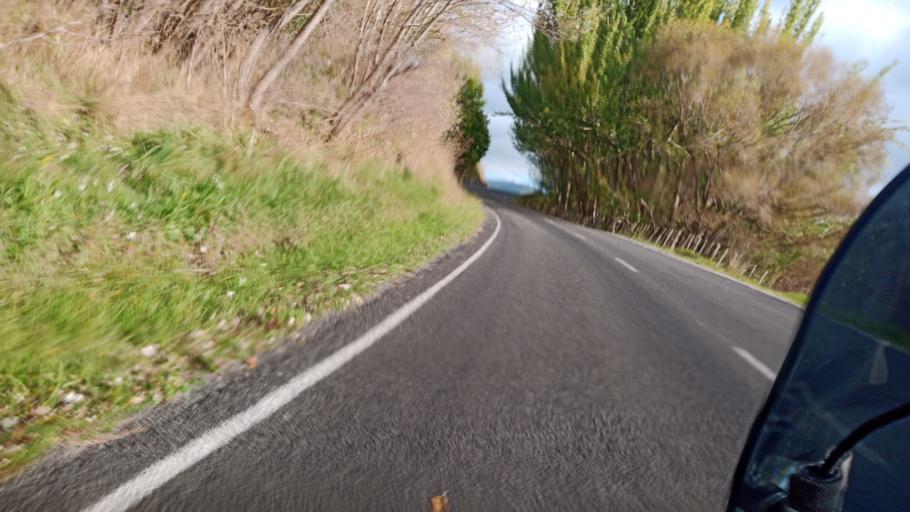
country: NZ
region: Gisborne
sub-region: Gisborne District
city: Gisborne
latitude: -38.5514
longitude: 177.6933
